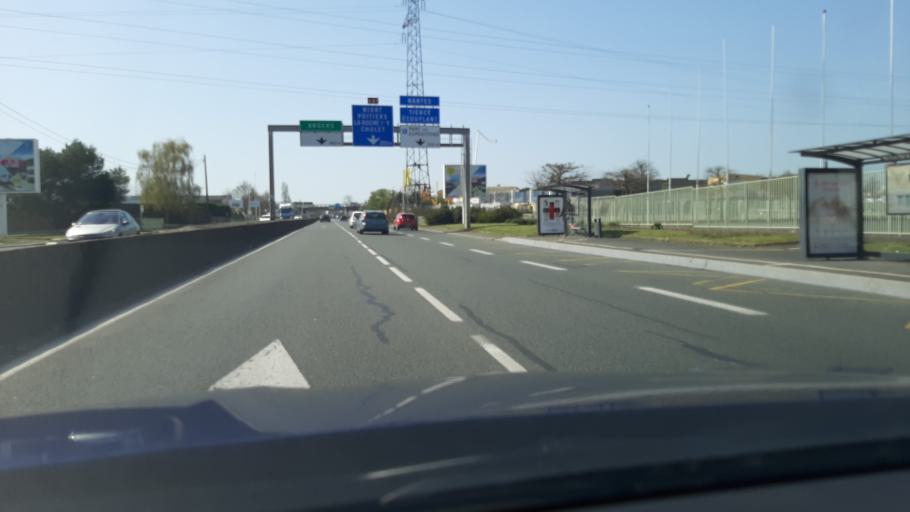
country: FR
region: Pays de la Loire
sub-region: Departement de Maine-et-Loire
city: Ecouflant
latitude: 47.4969
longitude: -0.4938
